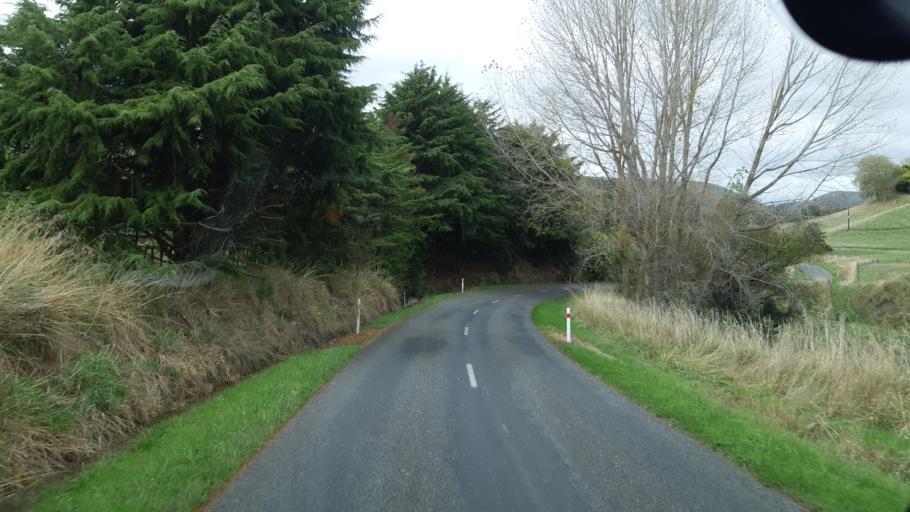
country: NZ
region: Manawatu-Wanganui
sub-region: Ruapehu District
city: Waiouru
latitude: -39.6131
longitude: 175.6715
